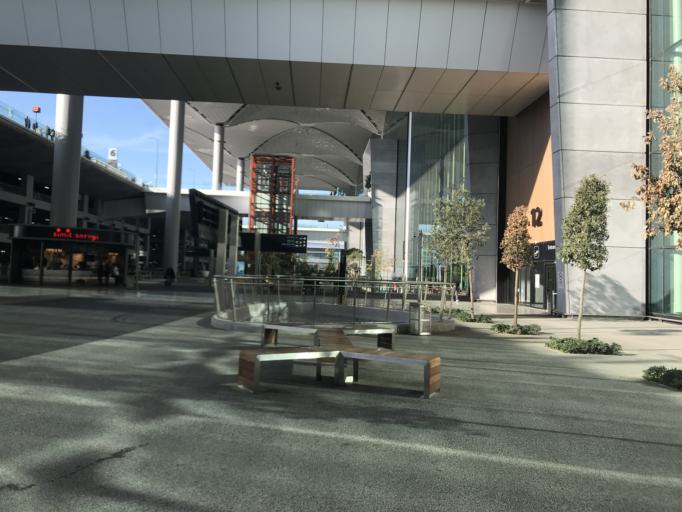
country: TR
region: Istanbul
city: Durusu
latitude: 41.2593
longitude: 28.7424
